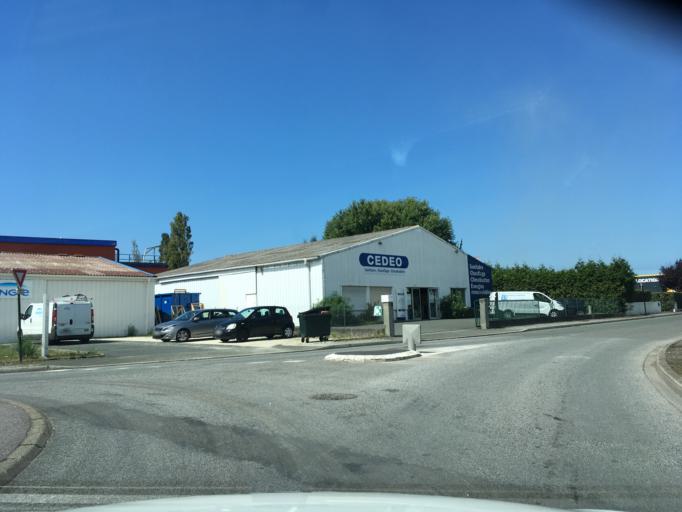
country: FR
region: Aquitaine
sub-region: Departement des Pyrenees-Atlantiques
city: Bayonne
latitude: 43.4874
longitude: -1.4507
